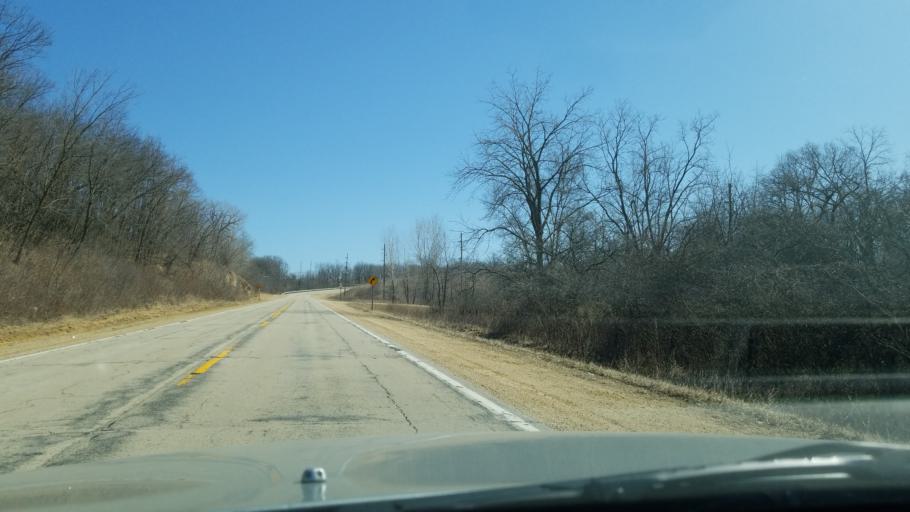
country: US
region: Wisconsin
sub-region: Iowa County
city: Mineral Point
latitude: 42.9043
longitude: -90.2312
